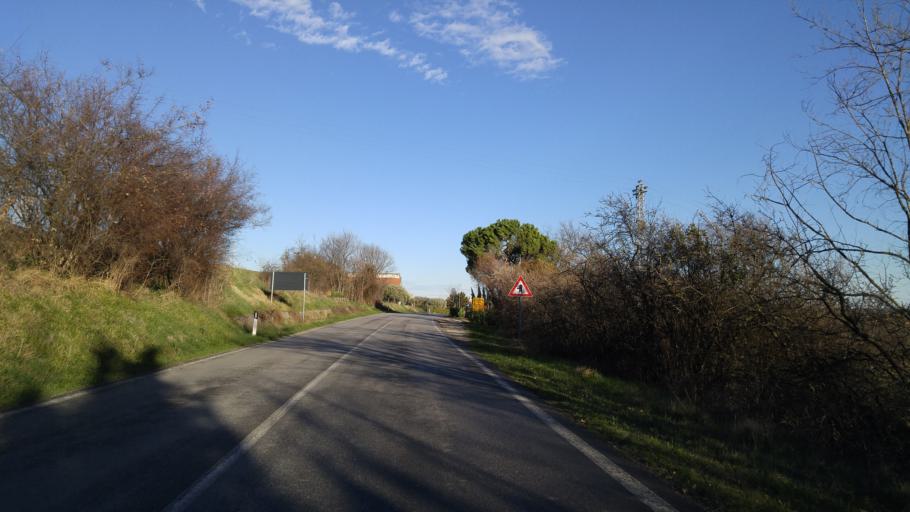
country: IT
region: The Marches
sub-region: Provincia di Pesaro e Urbino
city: Piagge
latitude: 43.7528
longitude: 12.9945
